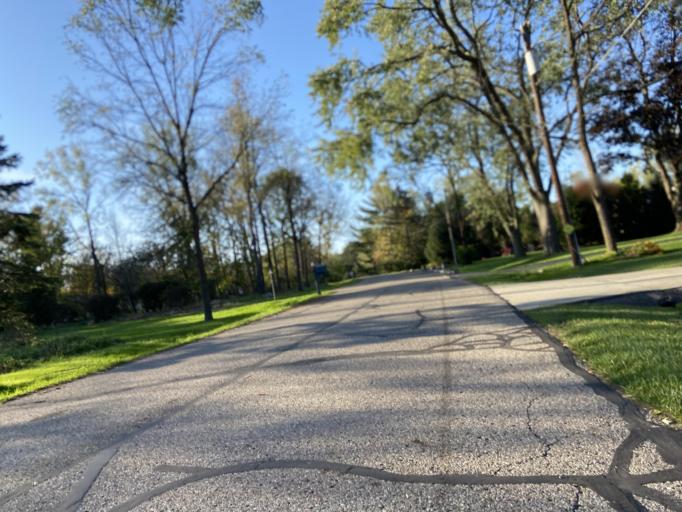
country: US
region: Michigan
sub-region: Oakland County
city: Franklin
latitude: 42.5084
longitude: -83.3295
